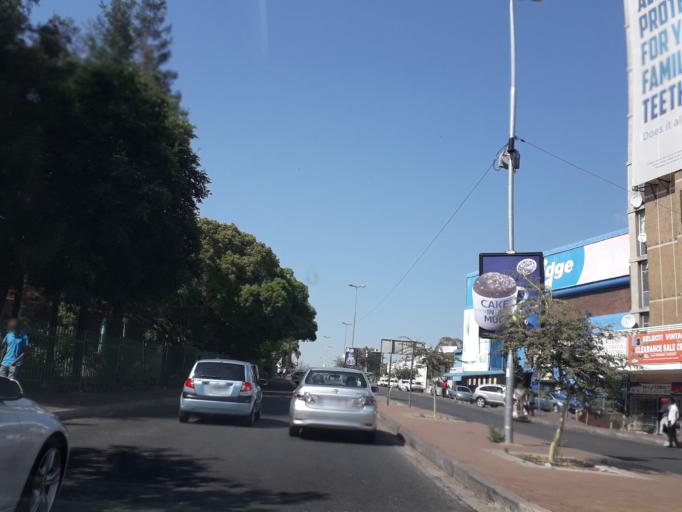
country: ZA
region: Gauteng
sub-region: City of Johannesburg Metropolitan Municipality
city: Johannesburg
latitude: -26.0941
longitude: 28.0057
